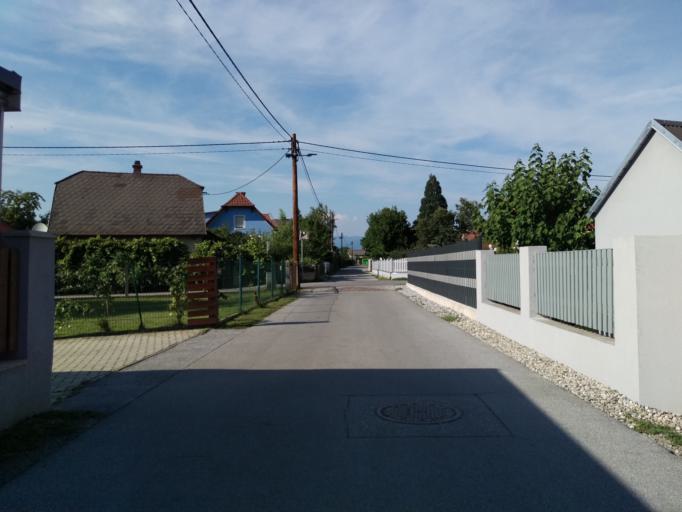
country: AT
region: Styria
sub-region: Politischer Bezirk Graz-Umgebung
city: Feldkirchen bei Graz
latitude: 47.0174
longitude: 15.4281
